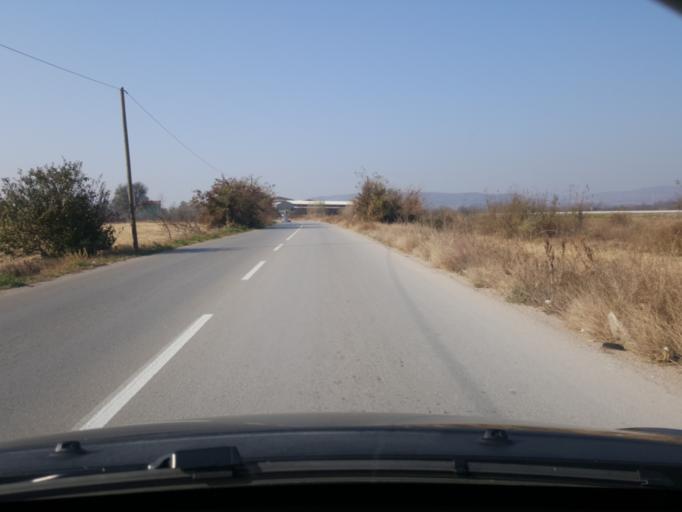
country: RS
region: Central Serbia
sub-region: Nisavski Okrug
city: Niska Banja
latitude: 43.3268
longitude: 21.9618
